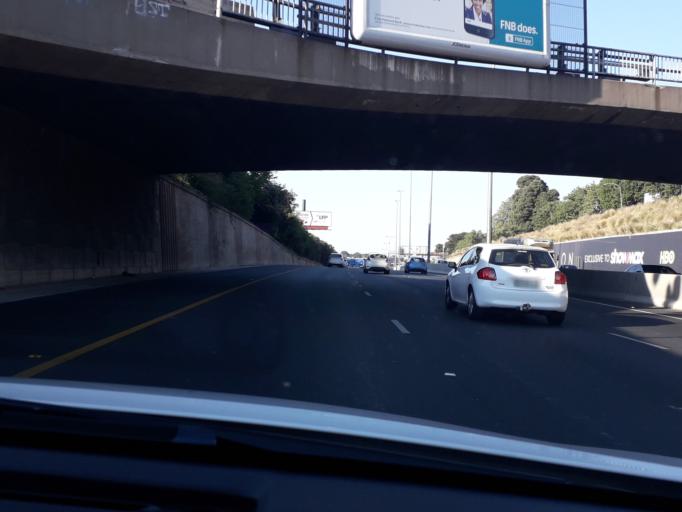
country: ZA
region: Gauteng
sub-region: City of Johannesburg Metropolitan Municipality
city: Johannesburg
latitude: -26.1784
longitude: 28.0368
